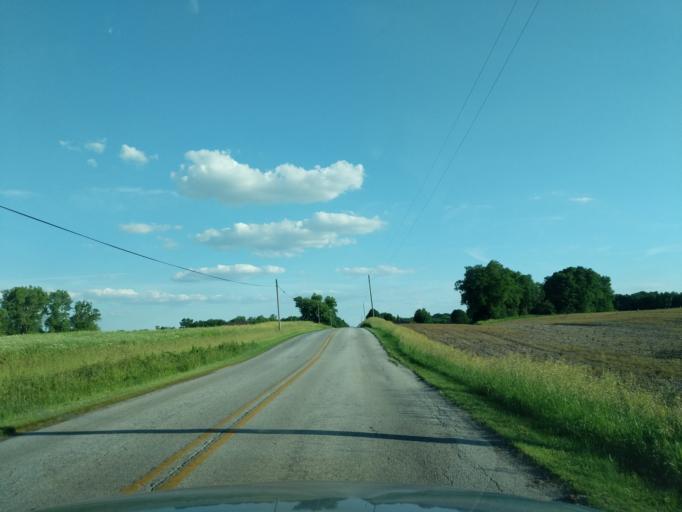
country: US
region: Indiana
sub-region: Huntington County
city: Huntington
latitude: 40.9076
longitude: -85.4714
